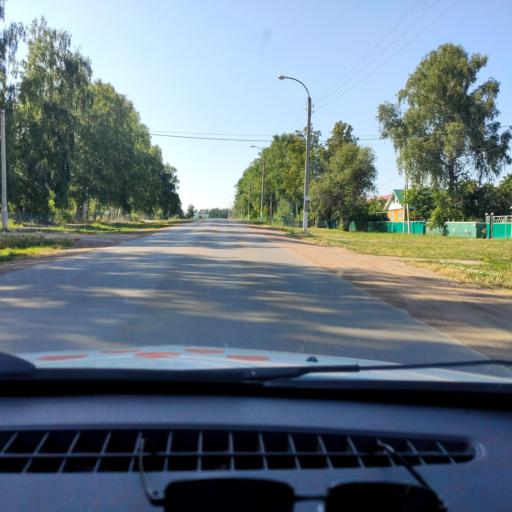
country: RU
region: Bashkortostan
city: Tolbazy
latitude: 54.0069
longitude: 55.8918
